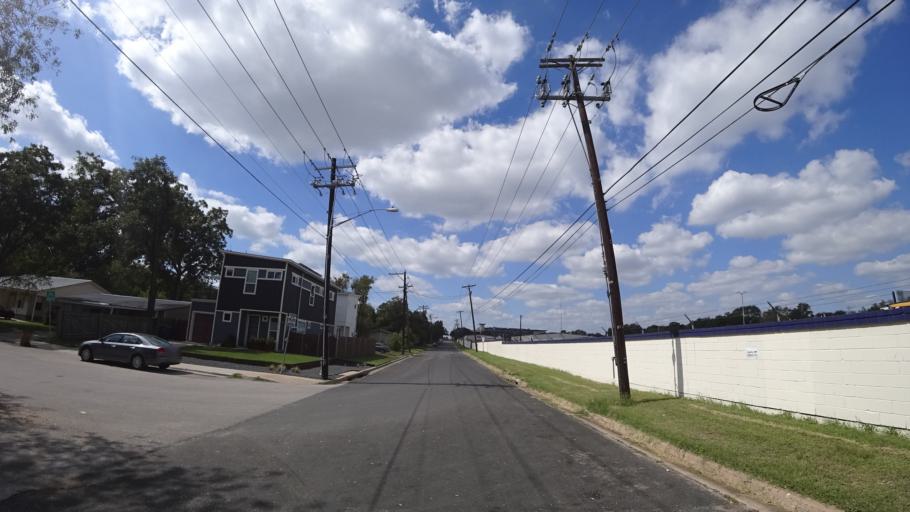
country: US
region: Texas
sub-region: Travis County
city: Austin
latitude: 30.3197
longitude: -97.7163
